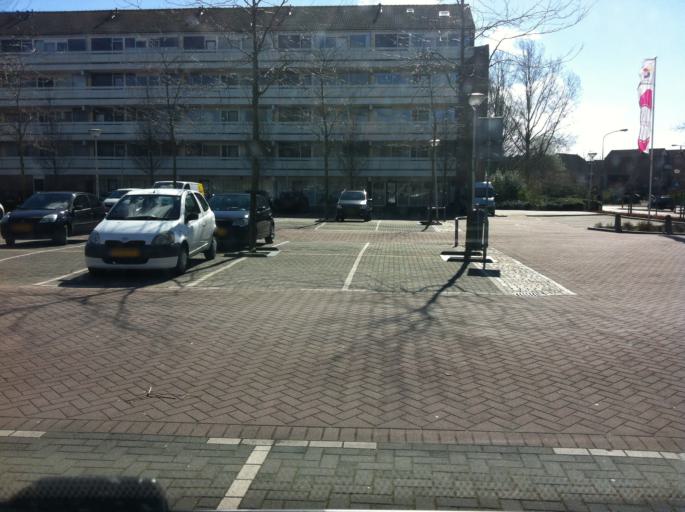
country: NL
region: South Holland
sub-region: Gemeente Gouda
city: Bloemendaal
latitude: 52.0322
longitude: 4.7021
